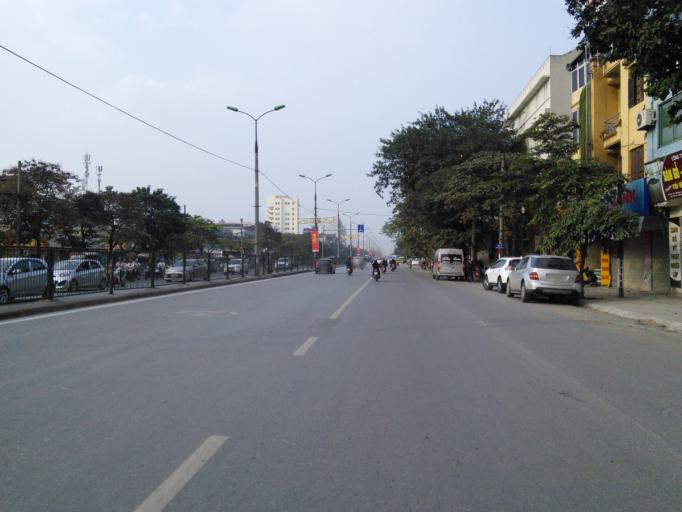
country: VN
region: Ha Noi
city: Hai BaTrung
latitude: 20.9870
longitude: 105.8412
